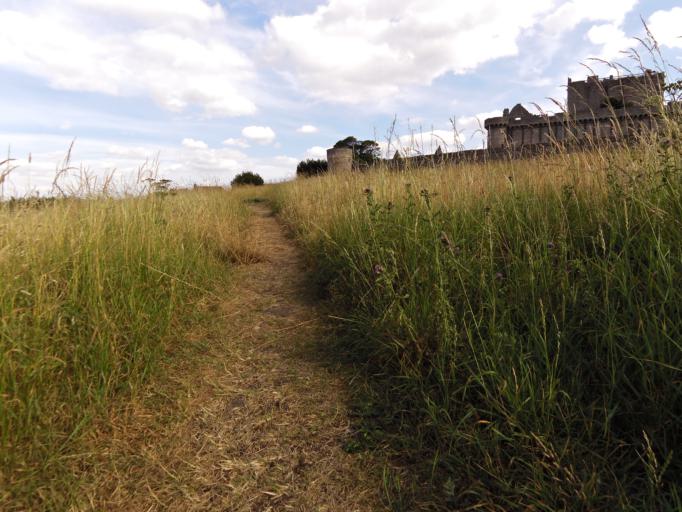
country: GB
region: Scotland
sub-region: West Lothian
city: Seafield
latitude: 55.9265
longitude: -3.1409
